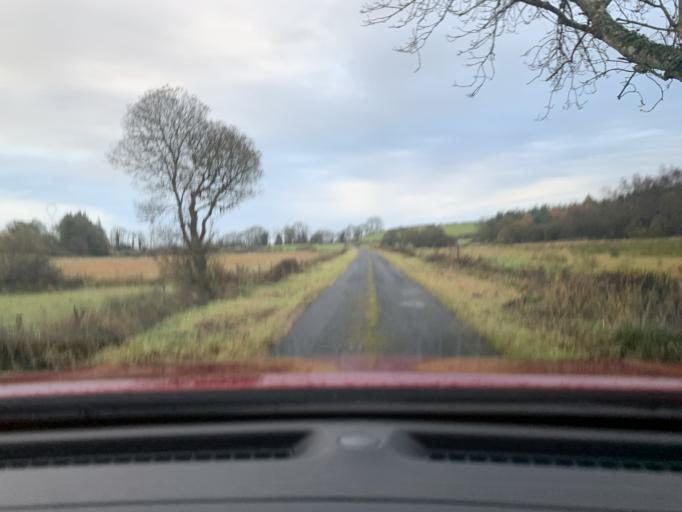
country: IE
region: Connaught
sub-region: Sligo
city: Ballymote
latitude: 54.0103
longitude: -8.4905
